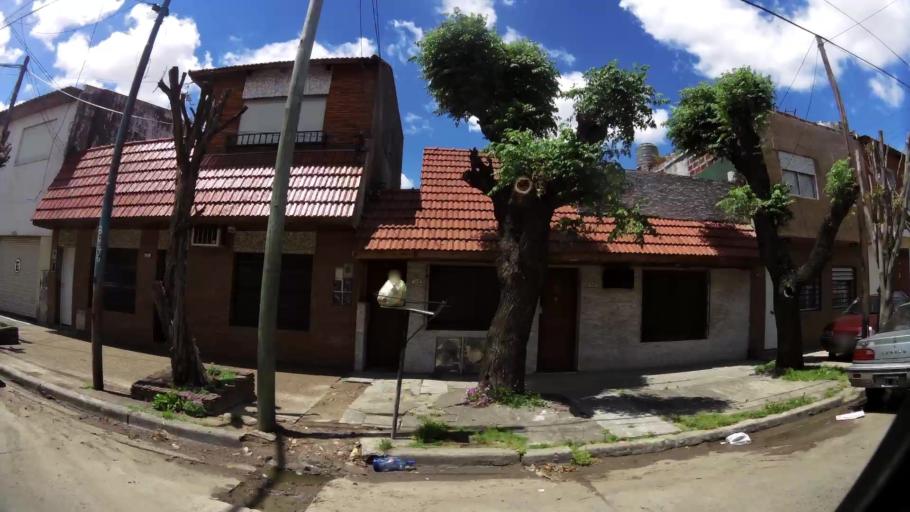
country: AR
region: Buenos Aires
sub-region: Partido de Lanus
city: Lanus
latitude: -34.7113
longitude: -58.4094
